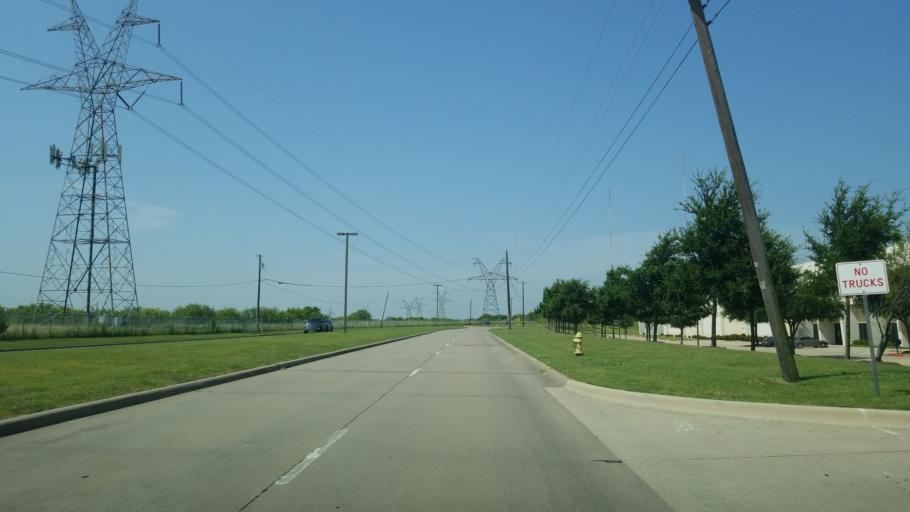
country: US
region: Texas
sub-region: Dallas County
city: Coppell
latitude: 32.9505
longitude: -96.9847
